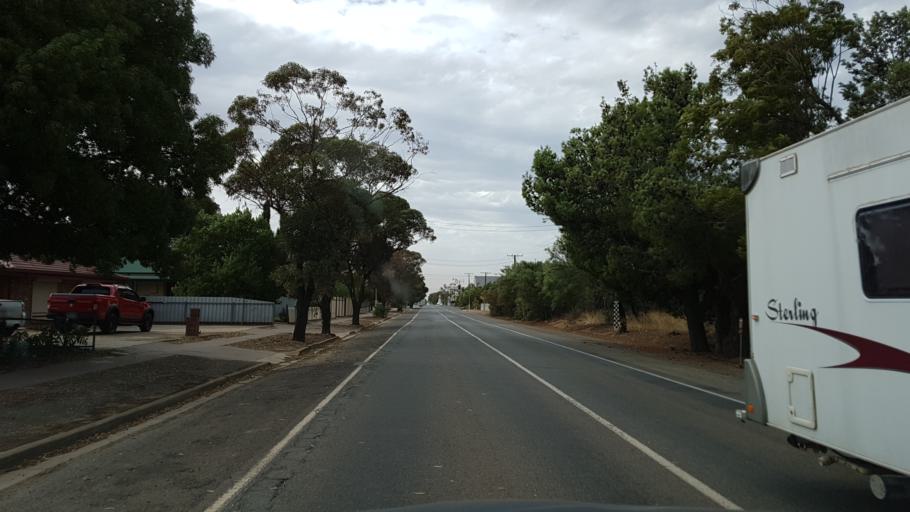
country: AU
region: South Australia
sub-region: Mallala
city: Mallala
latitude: -34.4357
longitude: 138.5053
